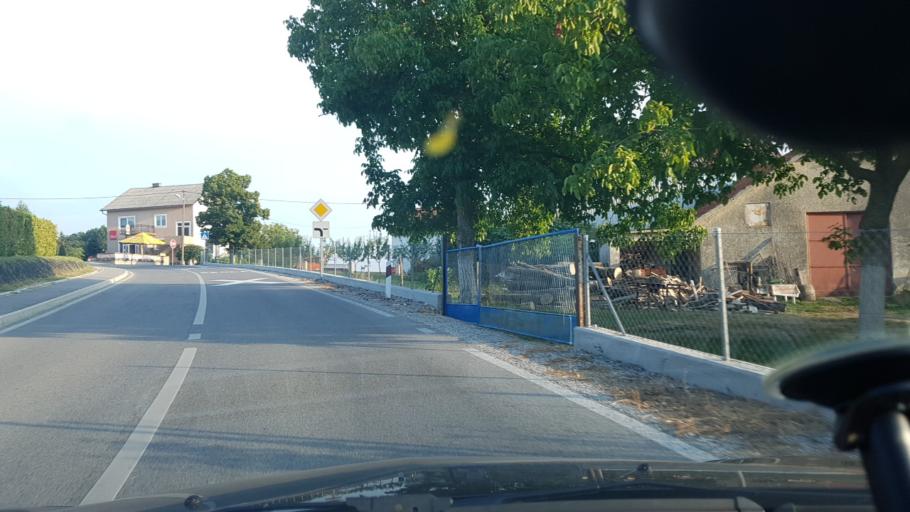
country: HR
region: Krapinsko-Zagorska
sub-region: Grad Krapina
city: Krapina
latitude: 46.1685
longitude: 15.8426
